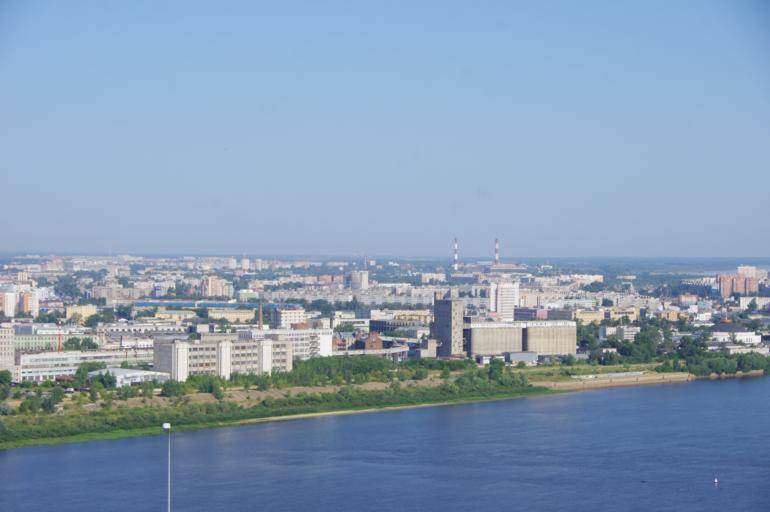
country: RU
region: Nizjnij Novgorod
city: Nizhniy Novgorod
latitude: 56.3034
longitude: 43.9728
